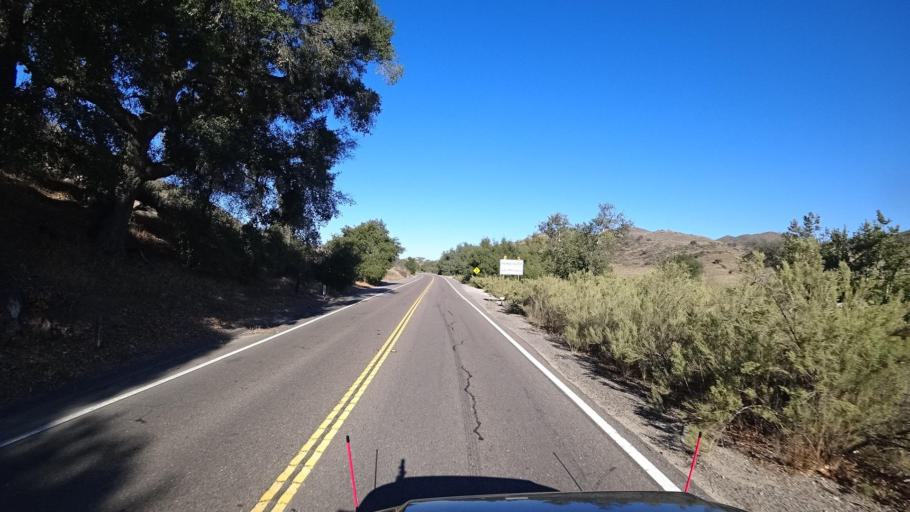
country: US
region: California
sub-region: San Diego County
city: Jamul
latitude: 32.6628
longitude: -116.8130
